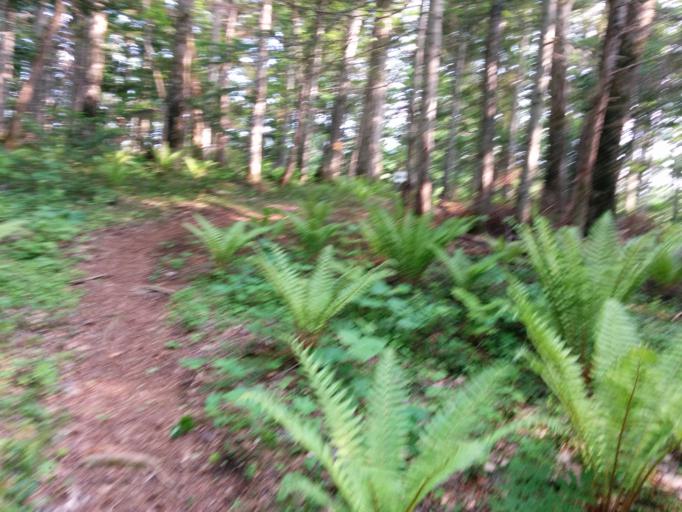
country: JP
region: Hokkaido
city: Bihoro
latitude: 43.4351
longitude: 144.1037
